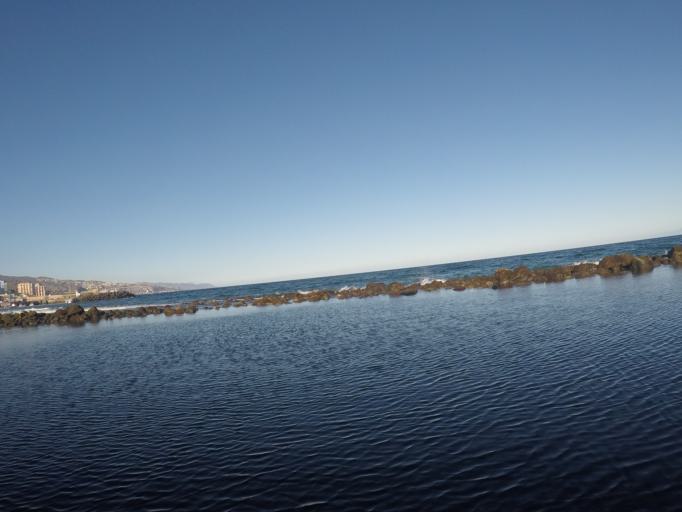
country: ES
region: Canary Islands
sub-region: Provincia de Santa Cruz de Tenerife
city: Candelaria
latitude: 28.3543
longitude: -16.3696
